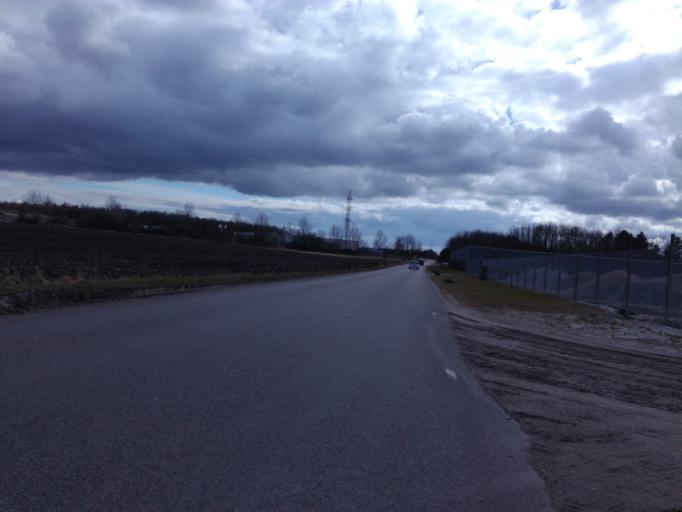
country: DK
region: South Denmark
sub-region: Fredericia Kommune
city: Fredericia
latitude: 55.5893
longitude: 9.7350
